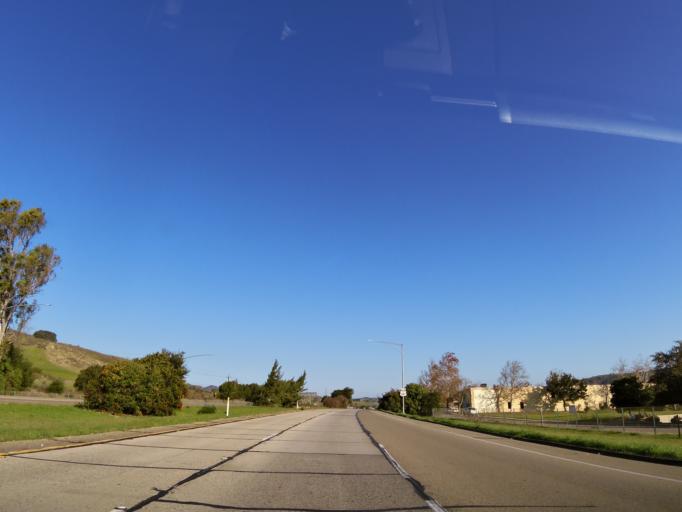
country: US
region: California
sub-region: Santa Barbara County
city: Buellton
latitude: 34.6211
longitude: -120.1892
